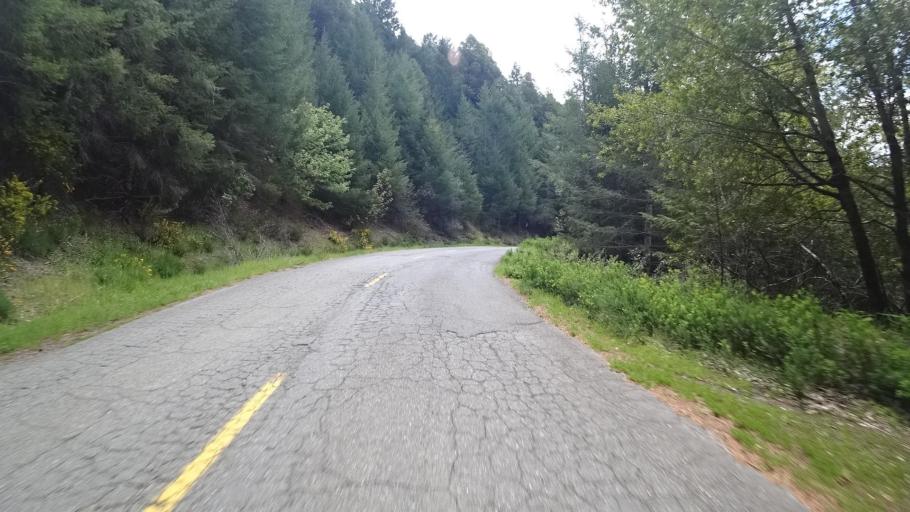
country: US
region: California
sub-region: Humboldt County
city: Redway
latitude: 40.0349
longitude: -123.9537
